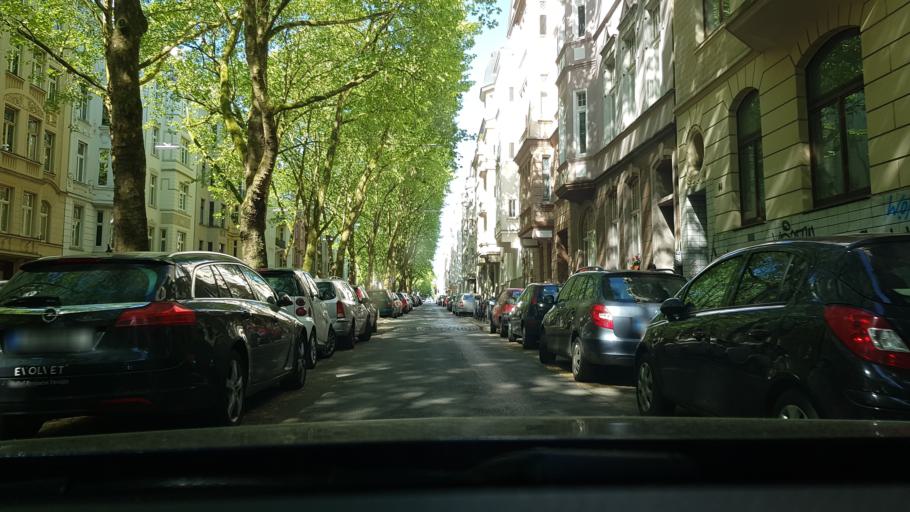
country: DE
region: North Rhine-Westphalia
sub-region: Regierungsbezirk Koln
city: Nippes
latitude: 50.9541
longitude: 6.9611
